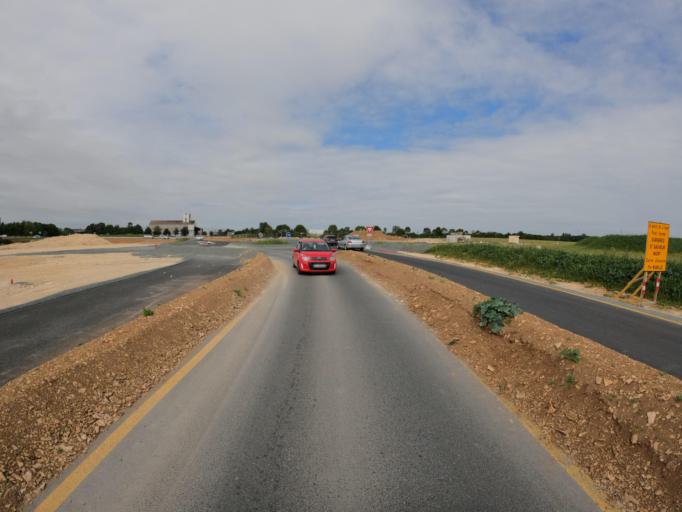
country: FR
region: Poitou-Charentes
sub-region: Departement de la Charente-Maritime
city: Saint-Jean-de-Liversay
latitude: 46.2296
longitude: -0.8769
